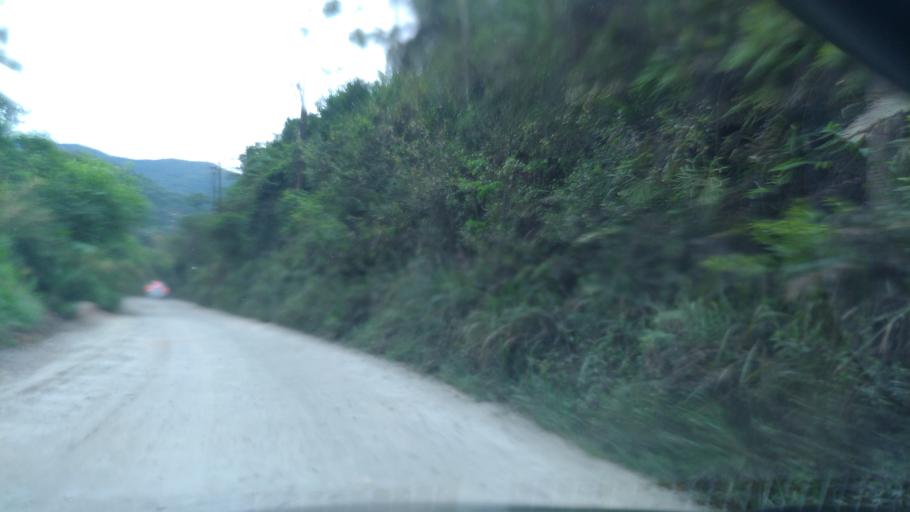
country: BR
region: Sao Paulo
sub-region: Sao Bernardo Do Campo
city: Sao Bernardo do Campo
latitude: -23.7411
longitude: -46.5154
